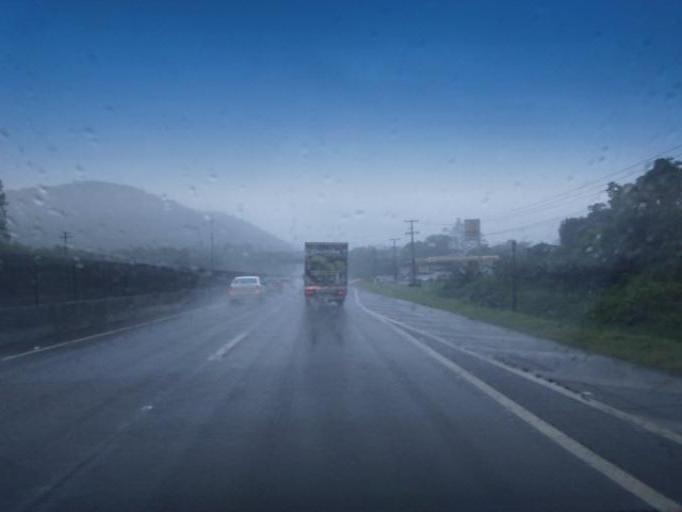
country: BR
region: Santa Catarina
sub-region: Joinville
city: Joinville
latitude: -26.2204
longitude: -48.9162
